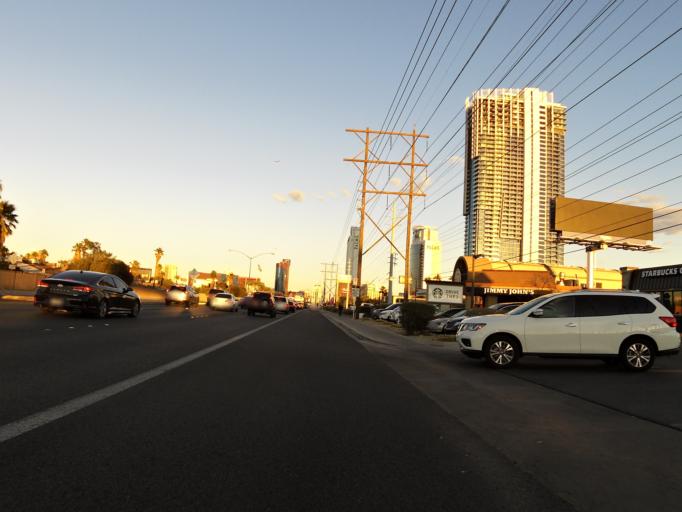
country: US
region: Nevada
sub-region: Clark County
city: Spring Valley
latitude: 36.1154
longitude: -115.2023
